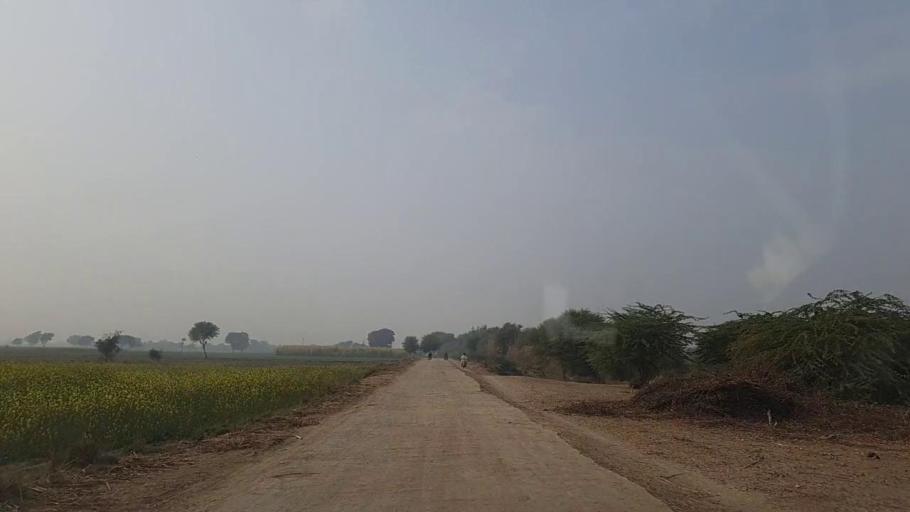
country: PK
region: Sindh
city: Sanghar
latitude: 26.0984
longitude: 68.8987
